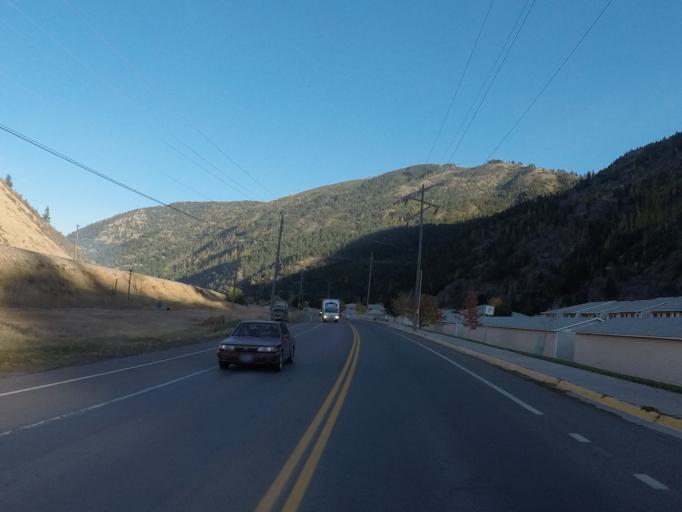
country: US
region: Montana
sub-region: Missoula County
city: Missoula
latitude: 46.8637
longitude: -113.9709
